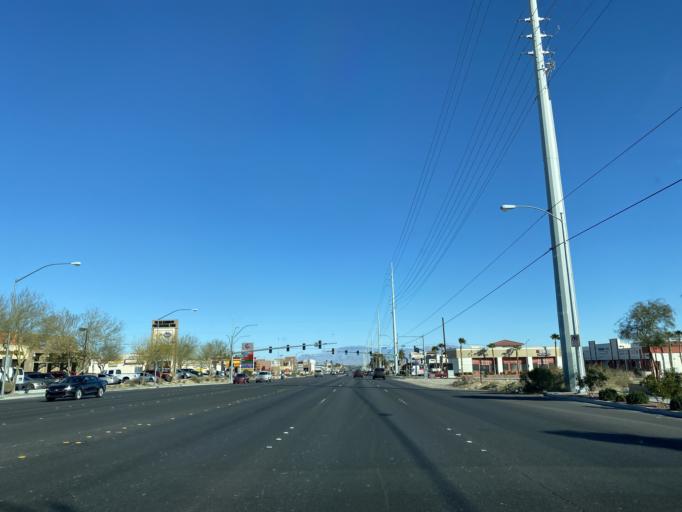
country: US
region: Nevada
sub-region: Clark County
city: Spring Valley
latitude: 36.0767
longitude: -115.2426
